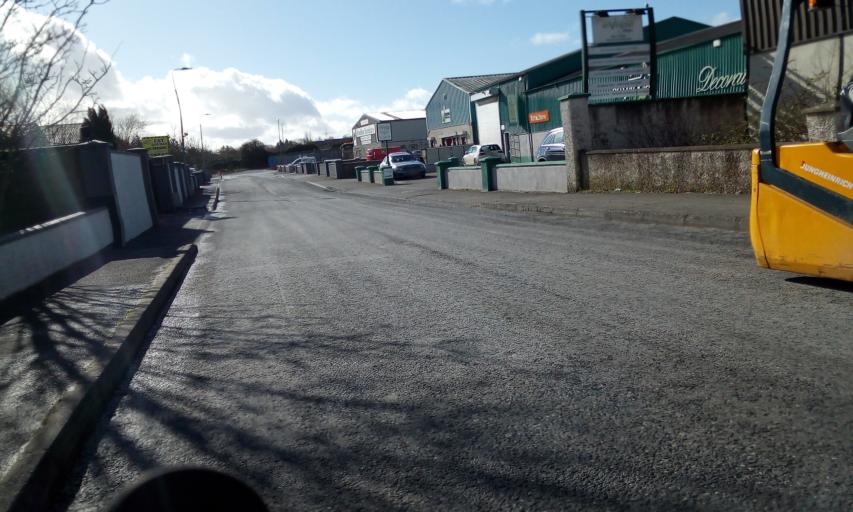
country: IE
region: Leinster
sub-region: Kilkenny
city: Kilkenny
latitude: 52.6544
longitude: -7.2277
